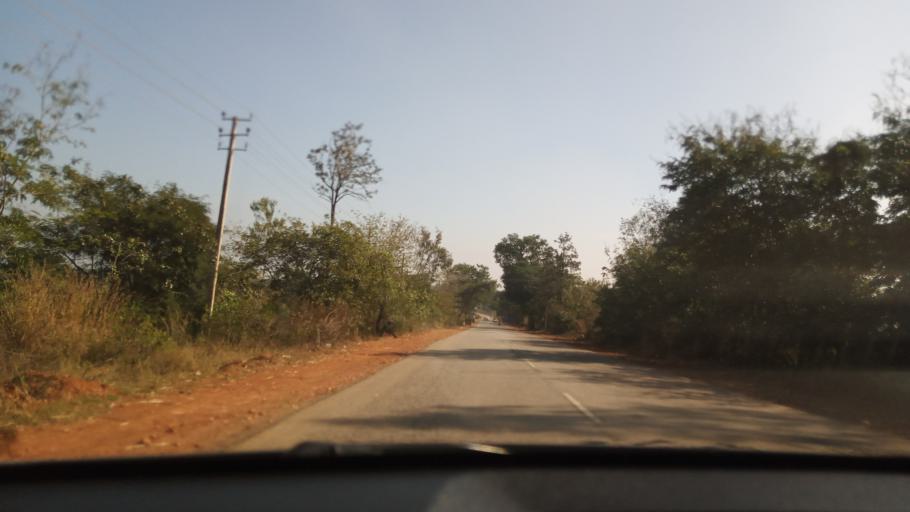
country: IN
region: Karnataka
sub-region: Bangalore Rural
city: Vijayapura
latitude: 13.2758
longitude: 77.7559
